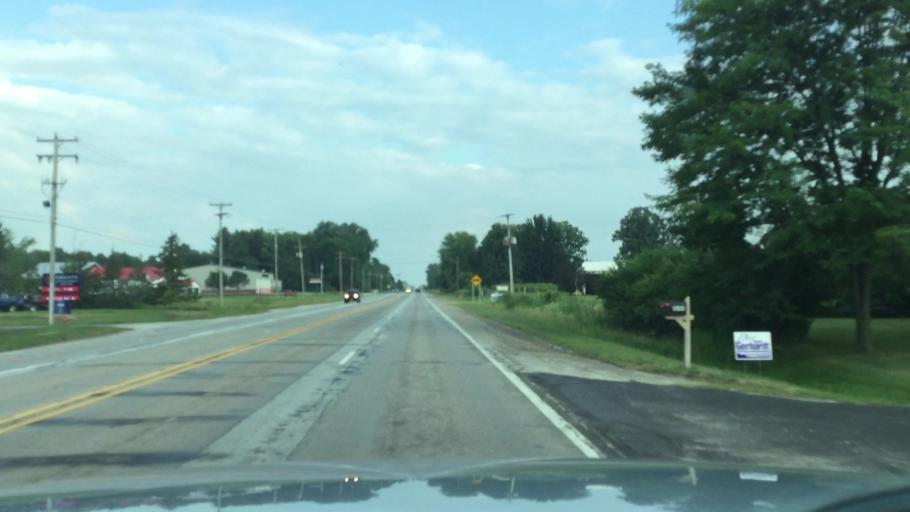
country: US
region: Michigan
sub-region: Saginaw County
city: Birch Run
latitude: 43.2636
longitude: -83.7796
